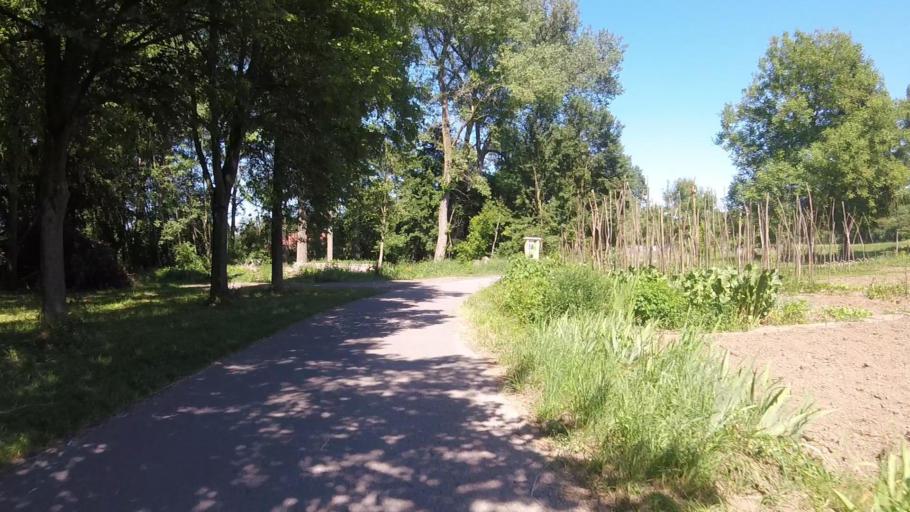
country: DE
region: Baden-Wuerttemberg
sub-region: Regierungsbezirk Stuttgart
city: Murr
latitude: 48.9585
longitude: 9.2615
